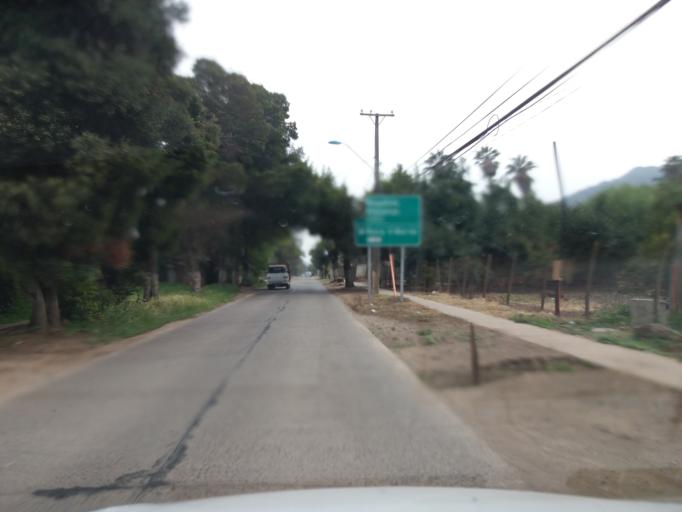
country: CL
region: Valparaiso
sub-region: Provincia de Quillota
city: Hacienda La Calera
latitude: -32.8177
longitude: -71.1355
